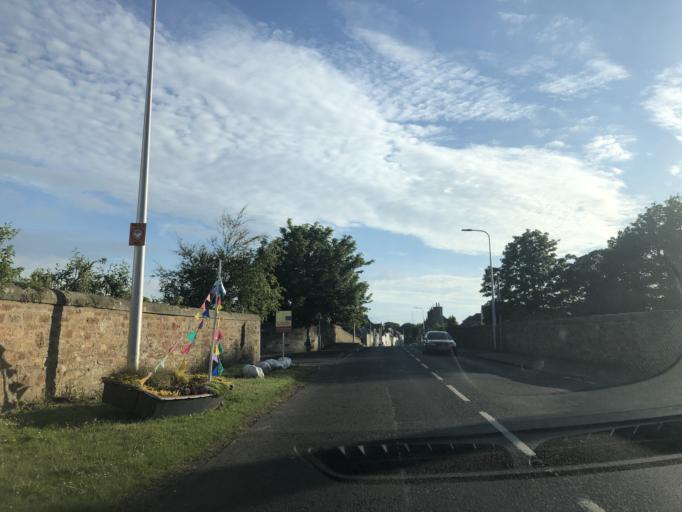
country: GB
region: Scotland
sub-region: Fife
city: Saint Monance
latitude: 56.1918
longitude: -2.8143
